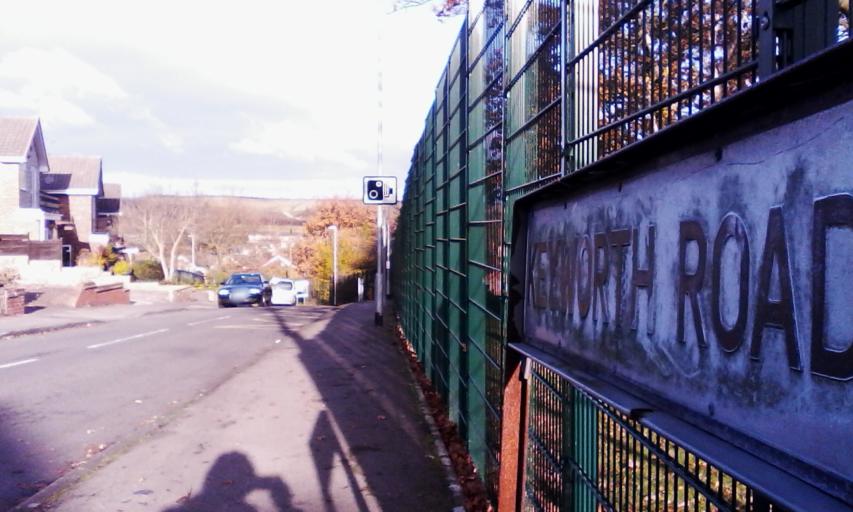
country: GB
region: England
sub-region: Nottinghamshire
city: Arnold
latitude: 52.9833
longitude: -1.0992
